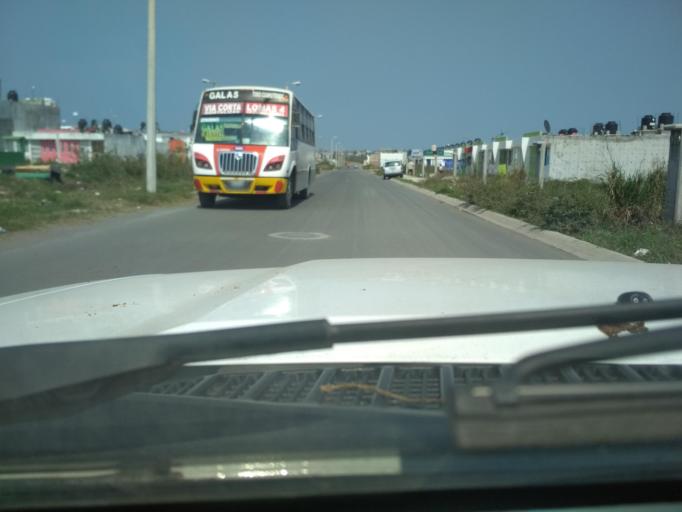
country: MX
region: Veracruz
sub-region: Veracruz
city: Lomas de Rio Medio Cuatro
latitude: 19.1889
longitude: -96.2106
